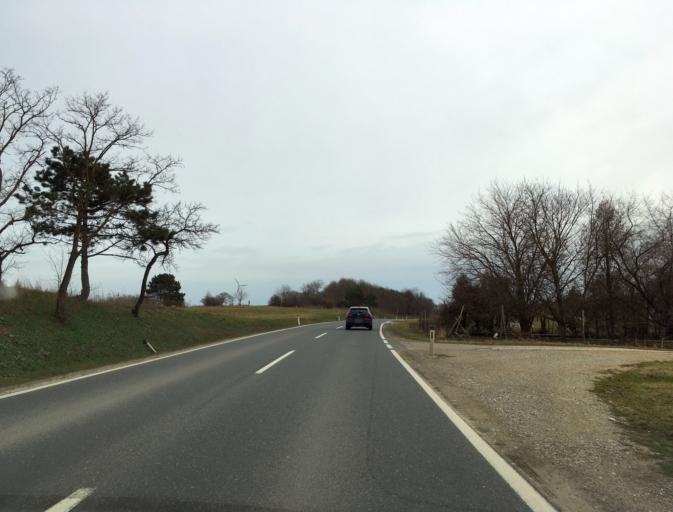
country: AT
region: Lower Austria
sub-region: Politischer Bezirk Ganserndorf
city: Parbasdorf
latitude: 48.2819
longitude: 16.5910
